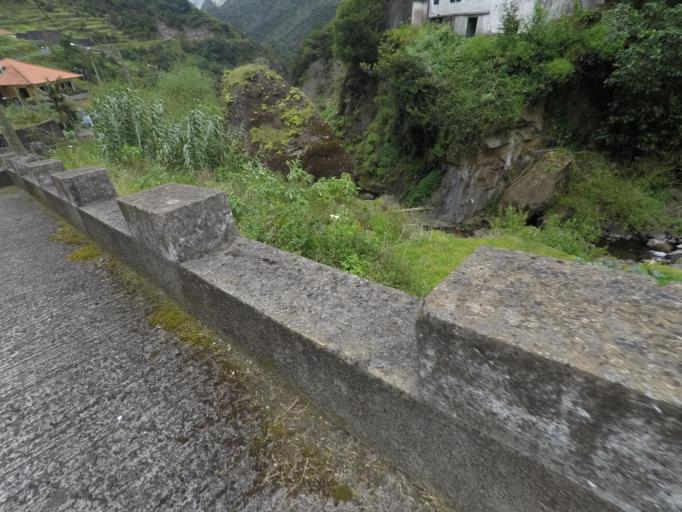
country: PT
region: Madeira
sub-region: Camara de Lobos
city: Curral das Freiras
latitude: 32.7817
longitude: -16.9789
